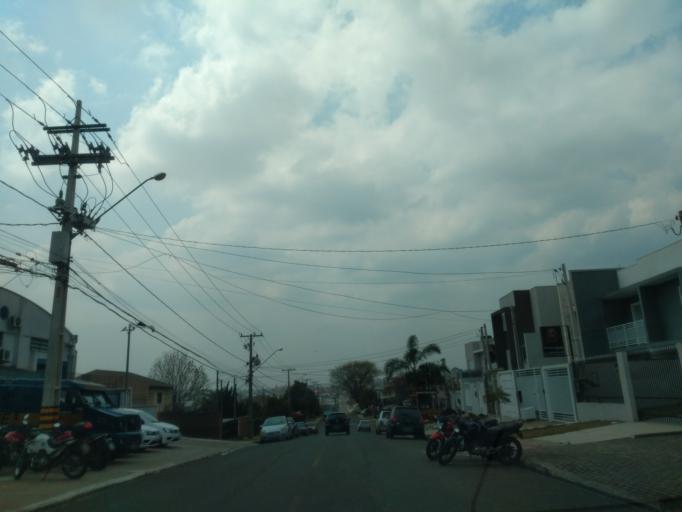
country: BR
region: Parana
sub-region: Guarapuava
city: Guarapuava
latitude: -25.3862
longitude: -51.4786
